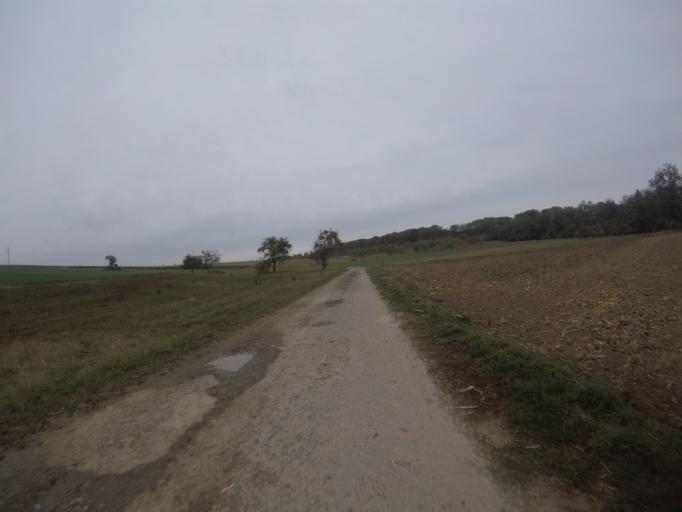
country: DE
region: Baden-Wuerttemberg
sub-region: Regierungsbezirk Stuttgart
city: Aspach
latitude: 48.9651
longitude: 9.3671
